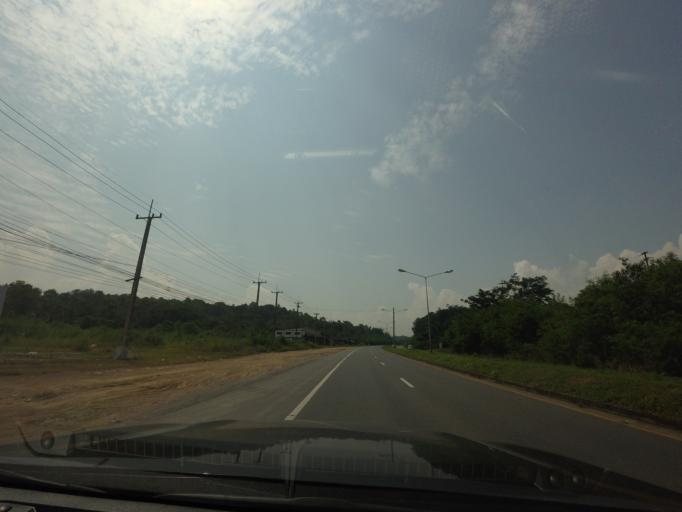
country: TH
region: Phrae
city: Den Chai
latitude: 17.9489
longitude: 100.0677
